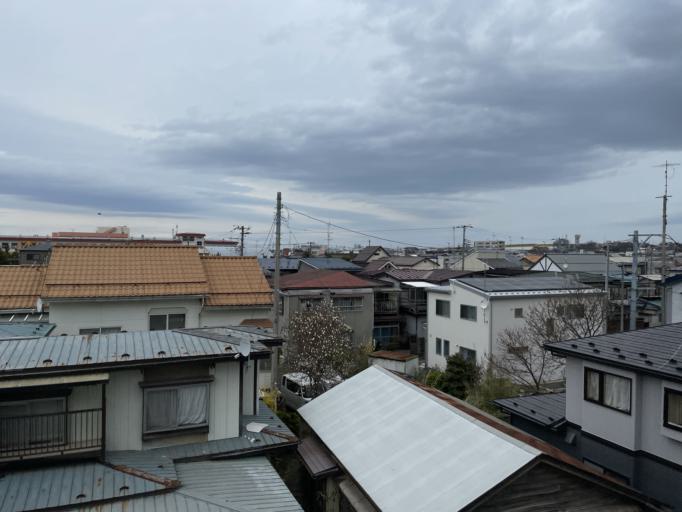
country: JP
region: Aomori
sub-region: Hachinohe Shi
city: Uchimaru
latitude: 40.5186
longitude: 141.5152
